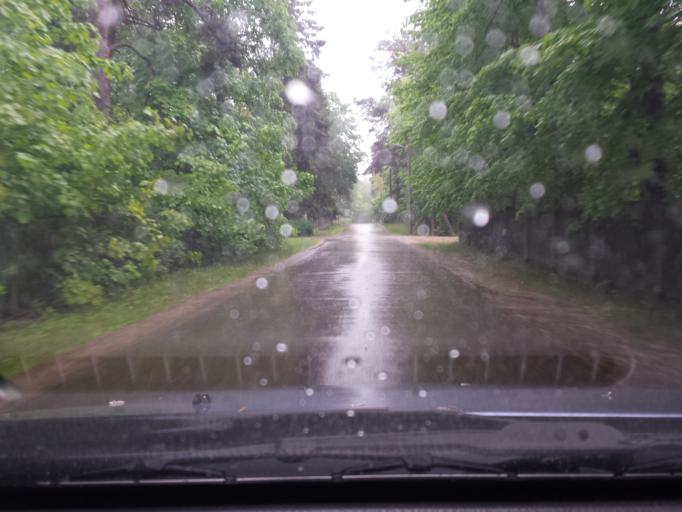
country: LV
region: Riga
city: Bolderaja
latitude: 57.0771
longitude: 24.1070
